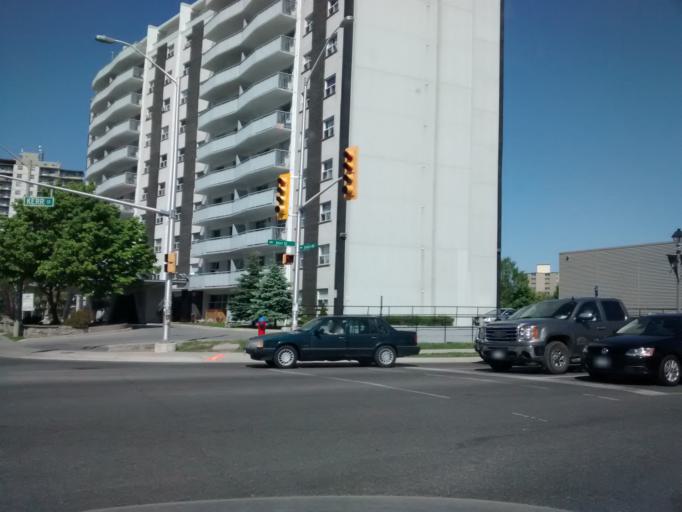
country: CA
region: Ontario
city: Oakville
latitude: 43.4466
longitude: -79.6869
